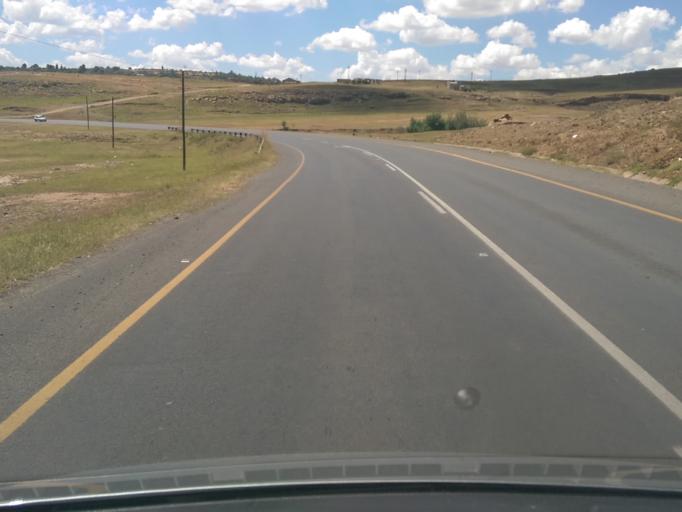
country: LS
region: Maseru
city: Maseru
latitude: -29.3894
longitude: 27.5047
